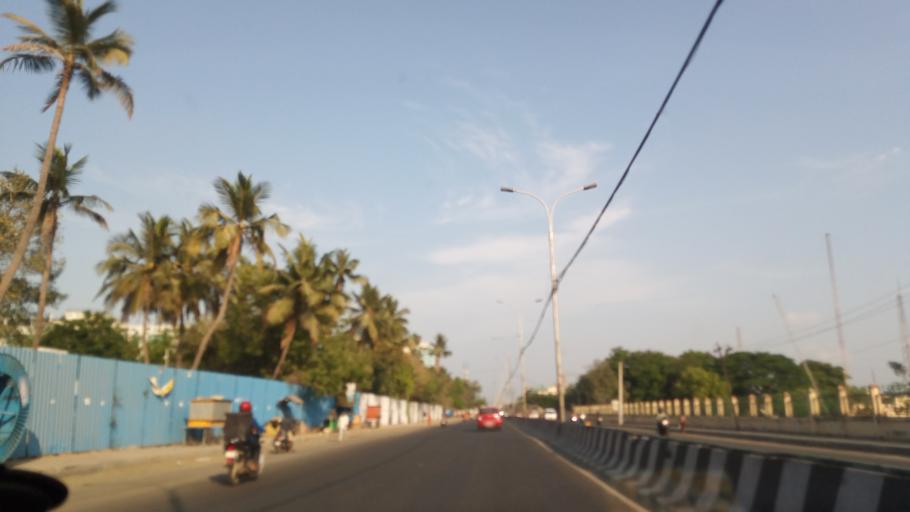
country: IN
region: Tamil Nadu
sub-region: Thiruvallur
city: Porur
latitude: 13.0311
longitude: 80.1657
